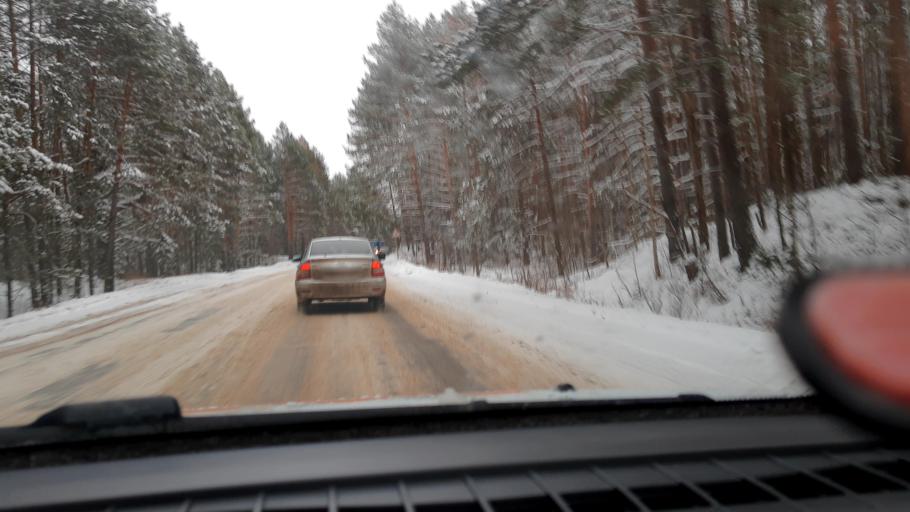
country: RU
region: Nizjnij Novgorod
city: Pamyat' Parizhskoy Kommuny
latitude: 56.2793
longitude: 44.3855
